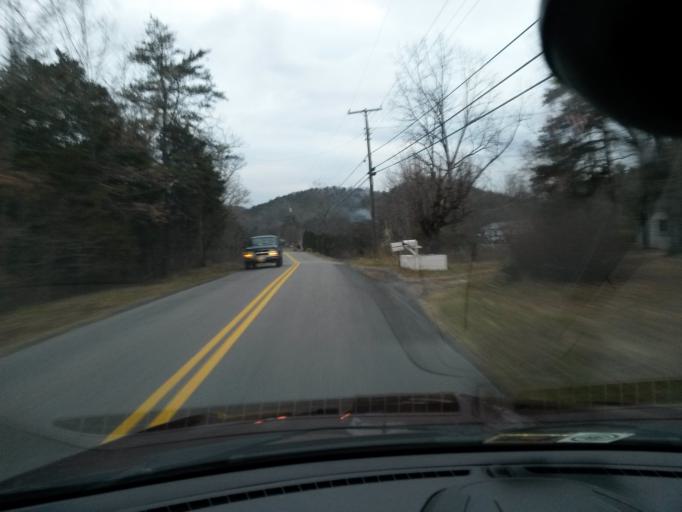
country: US
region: Virginia
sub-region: Alleghany County
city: Clifton Forge
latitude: 37.8374
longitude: -79.7925
